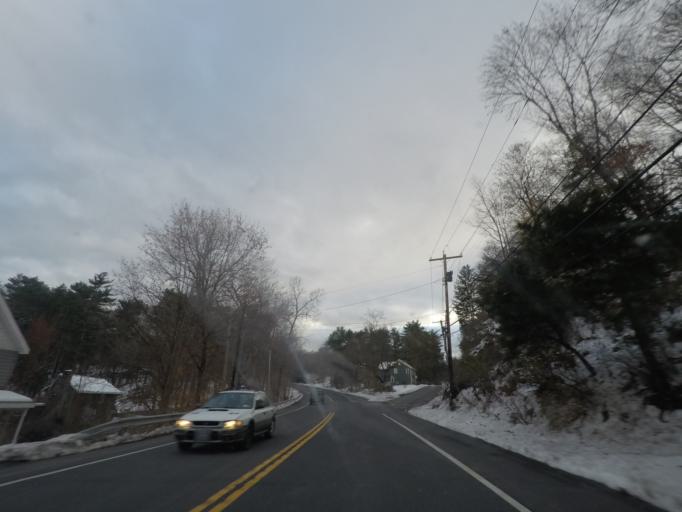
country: US
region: New York
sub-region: Ulster County
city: Hurley
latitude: 41.8862
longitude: -74.0451
